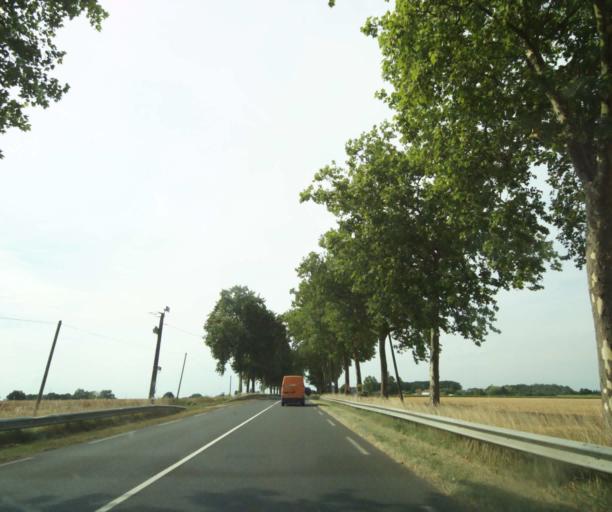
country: FR
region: Centre
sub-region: Departement d'Indre-et-Loire
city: Neuille-Pont-Pierre
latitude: 47.5392
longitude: 0.5575
